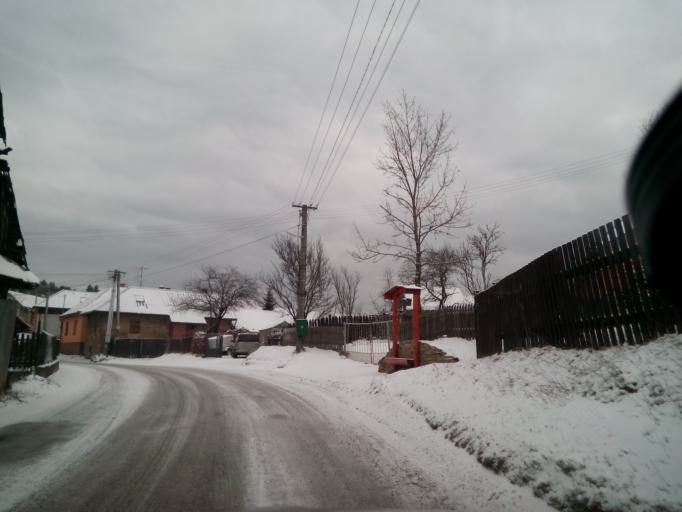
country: SK
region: Presovsky
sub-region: Okres Presov
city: Levoca
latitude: 49.0431
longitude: 20.6448
